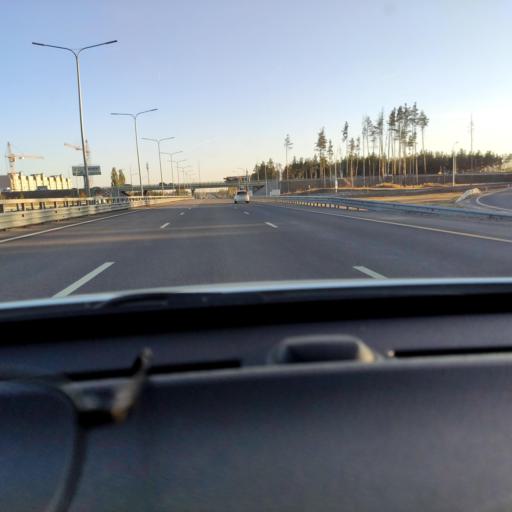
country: RU
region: Voronezj
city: Somovo
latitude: 51.7441
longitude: 39.3066
